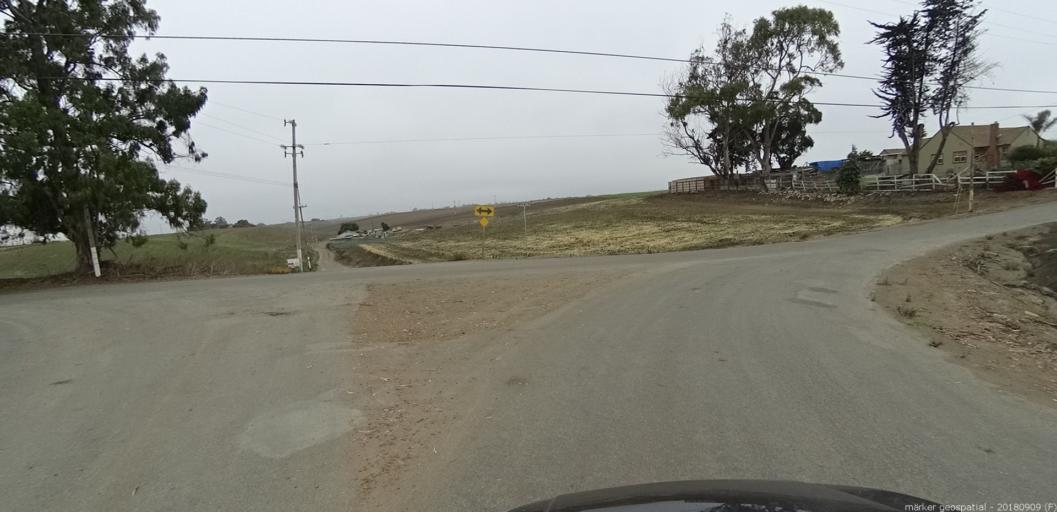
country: US
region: California
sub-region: Monterey County
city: Boronda
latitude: 36.7182
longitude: -121.6833
